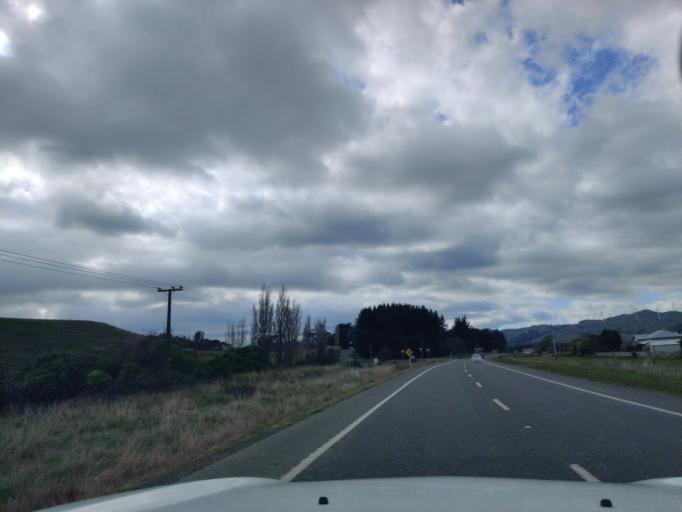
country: NZ
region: Manawatu-Wanganui
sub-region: Palmerston North City
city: Palmerston North
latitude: -40.3008
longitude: 175.7368
